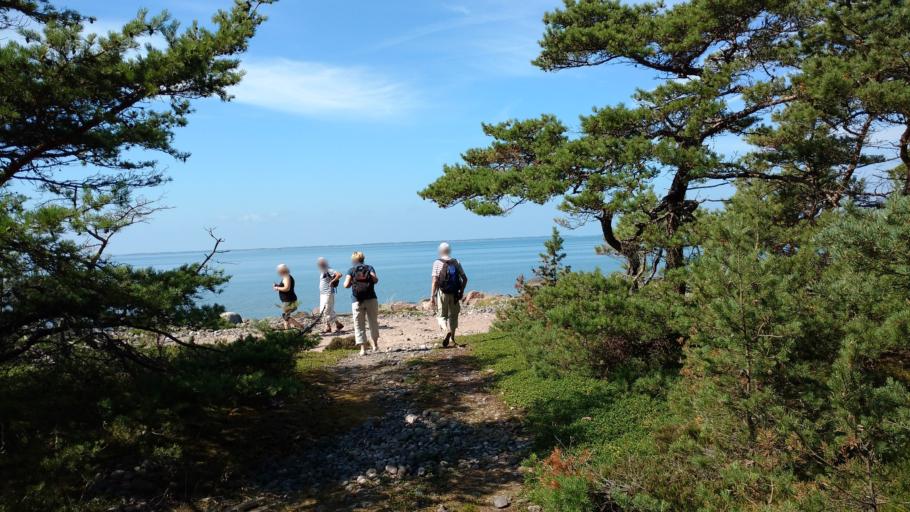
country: FI
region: Varsinais-Suomi
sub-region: Aboland-Turunmaa
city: Dragsfjaerd
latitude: 59.8102
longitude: 22.3158
